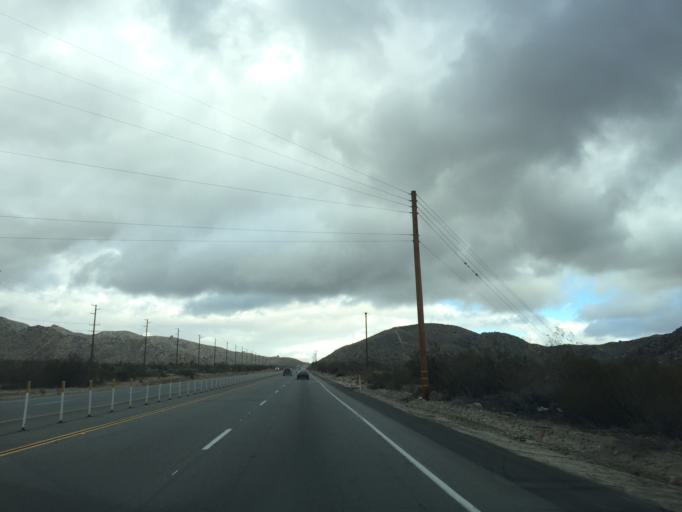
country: US
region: California
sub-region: San Bernardino County
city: Yucca Valley
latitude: 34.0973
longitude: -116.5052
